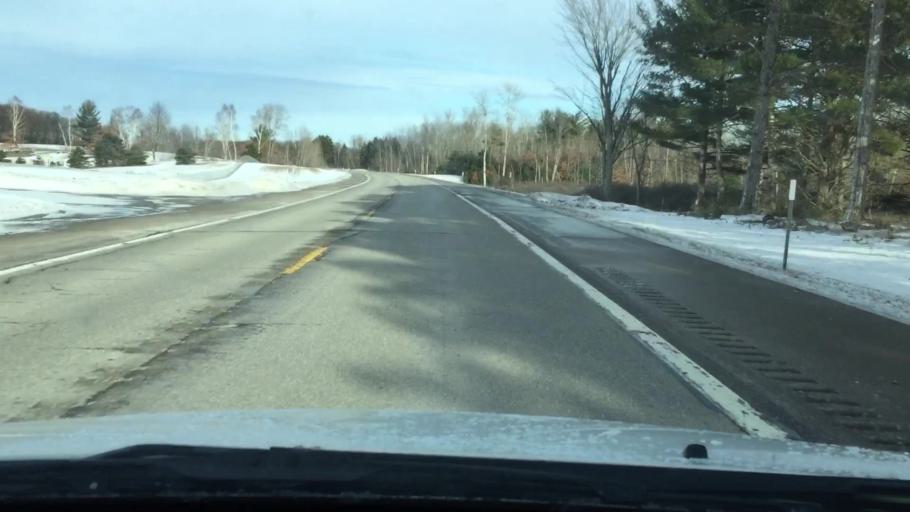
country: US
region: Michigan
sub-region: Wexford County
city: Manton
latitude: 44.5897
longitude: -85.3410
